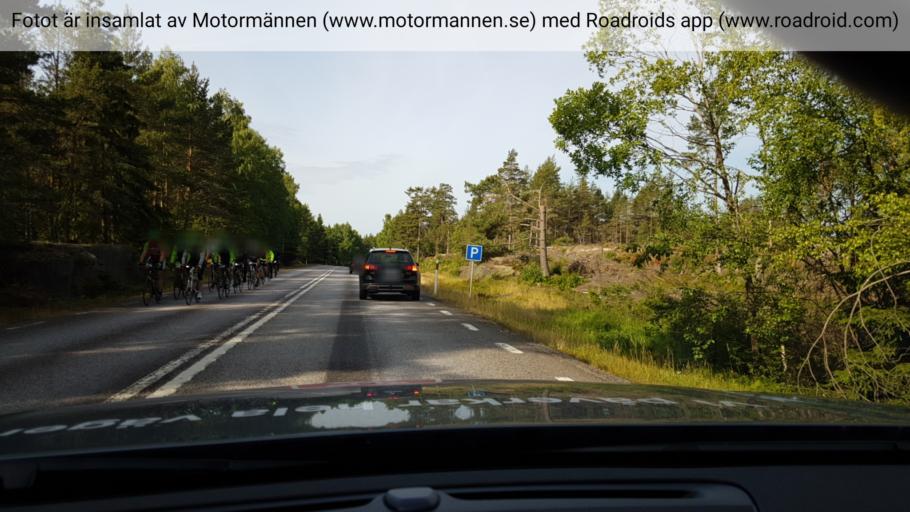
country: SE
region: OErebro
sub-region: Askersunds Kommun
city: Askersund
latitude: 58.7146
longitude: 14.7375
